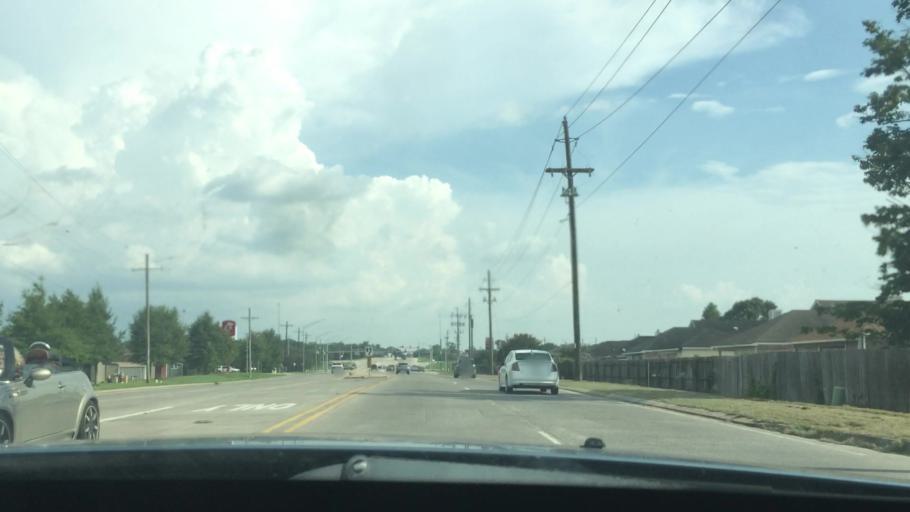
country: US
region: Louisiana
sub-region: East Baton Rouge Parish
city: Shenandoah
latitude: 30.4439
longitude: -91.0245
